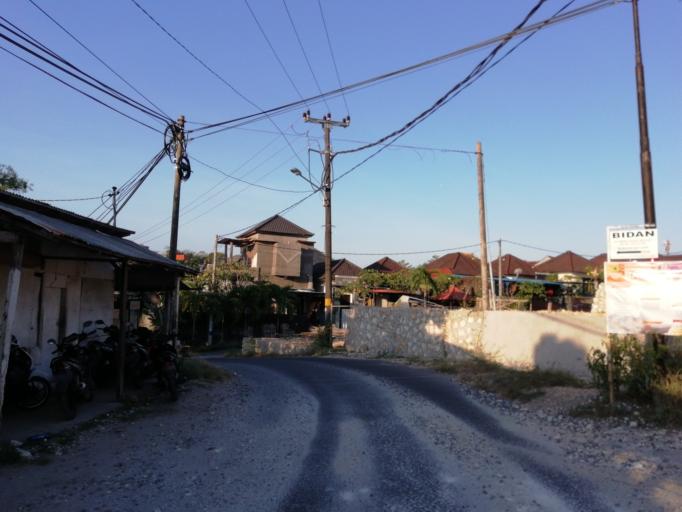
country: ID
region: Bali
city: Bualu
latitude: -8.8001
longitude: 115.1955
